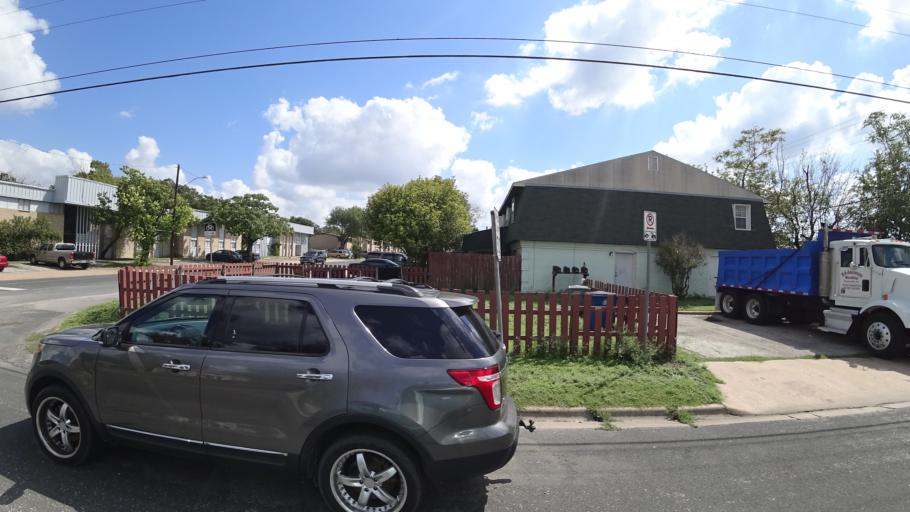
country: US
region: Texas
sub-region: Travis County
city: Austin
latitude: 30.3544
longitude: -97.7256
